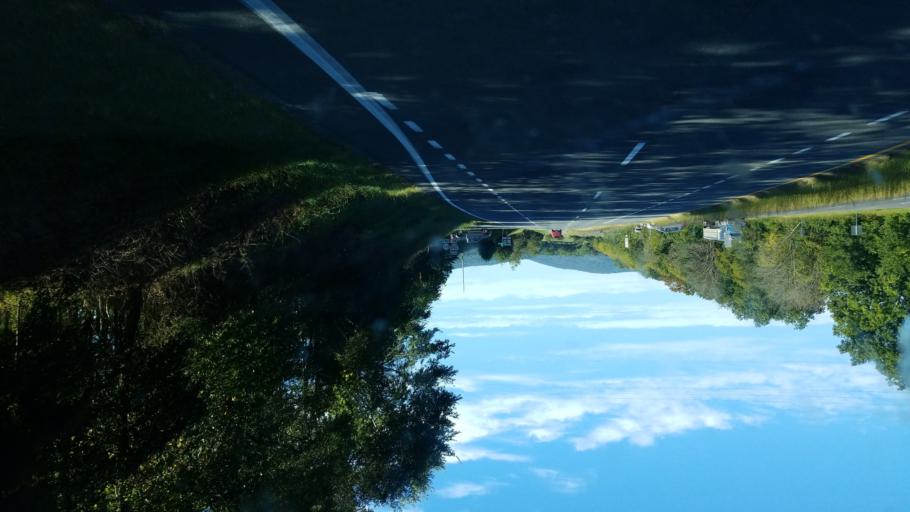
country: US
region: Virginia
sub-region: Warren County
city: Shenandoah Farms
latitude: 39.0593
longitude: -78.0421
